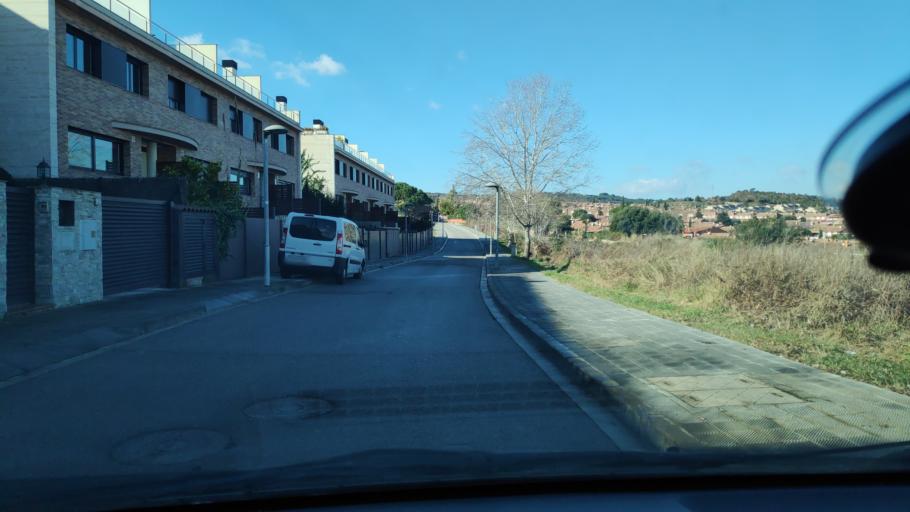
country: ES
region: Catalonia
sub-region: Provincia de Barcelona
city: Sant Quirze del Valles
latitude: 41.5251
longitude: 2.0766
